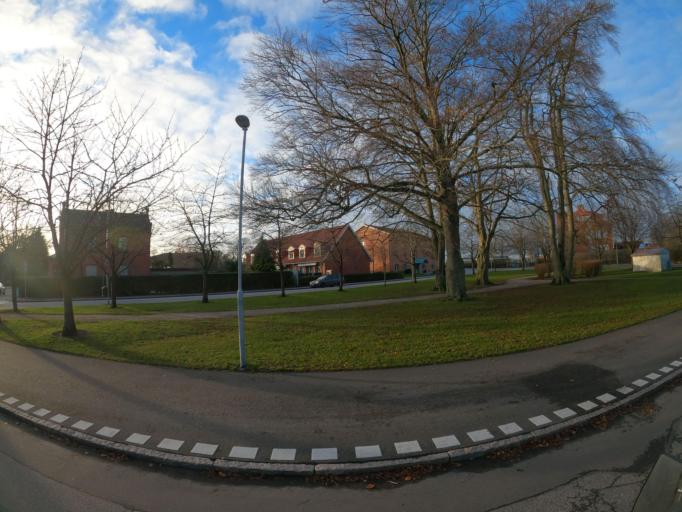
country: SE
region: Skane
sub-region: Svedala Kommun
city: Svedala
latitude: 55.5117
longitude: 13.2372
